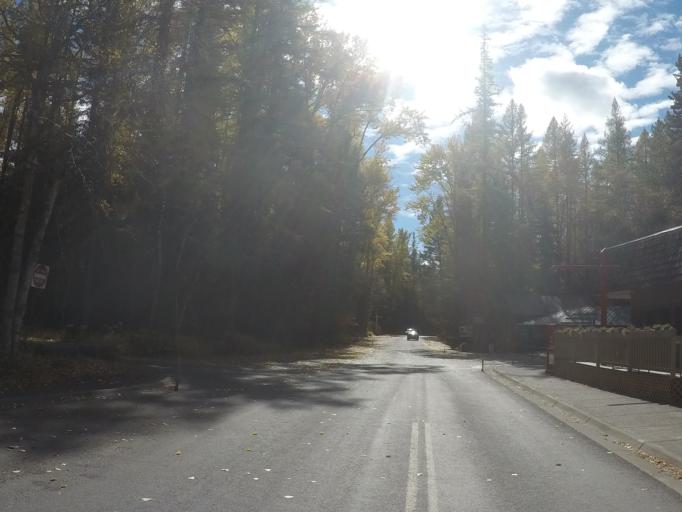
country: US
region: Montana
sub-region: Flathead County
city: Columbia Falls
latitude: 48.5278
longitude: -113.9938
